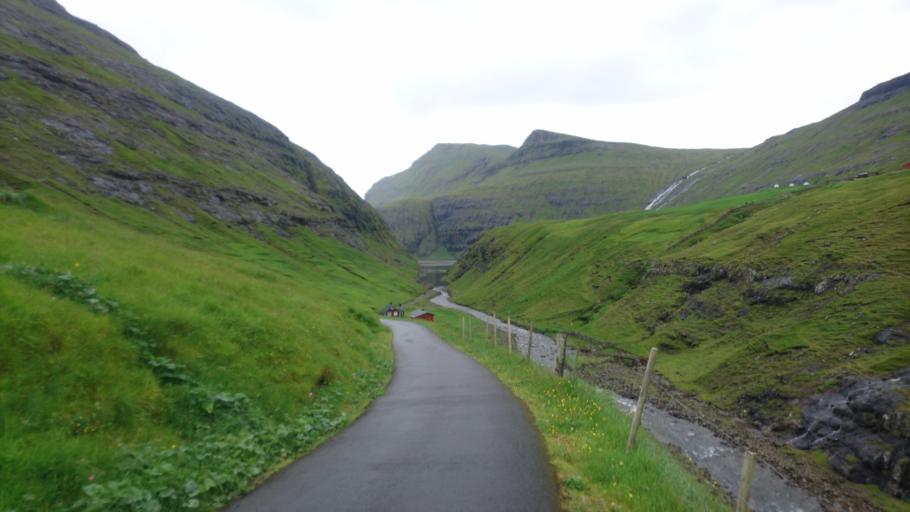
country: FO
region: Streymoy
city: Vestmanna
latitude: 62.2435
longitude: -7.1736
